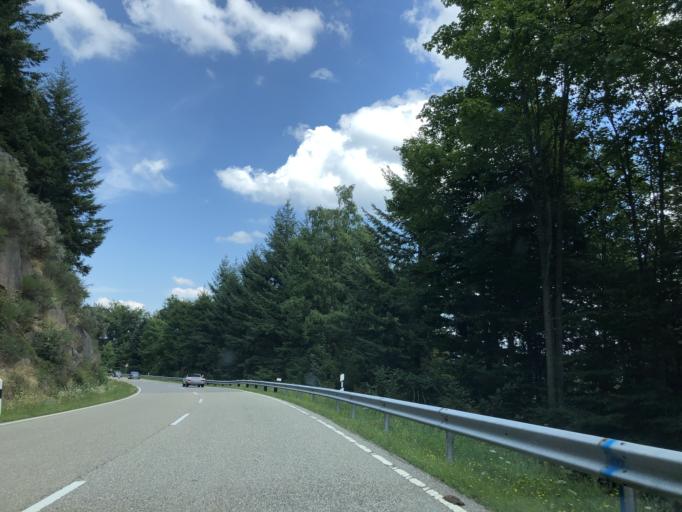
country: DE
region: Baden-Wuerttemberg
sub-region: Karlsruhe Region
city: Buhlertal
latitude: 48.6903
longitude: 8.2337
